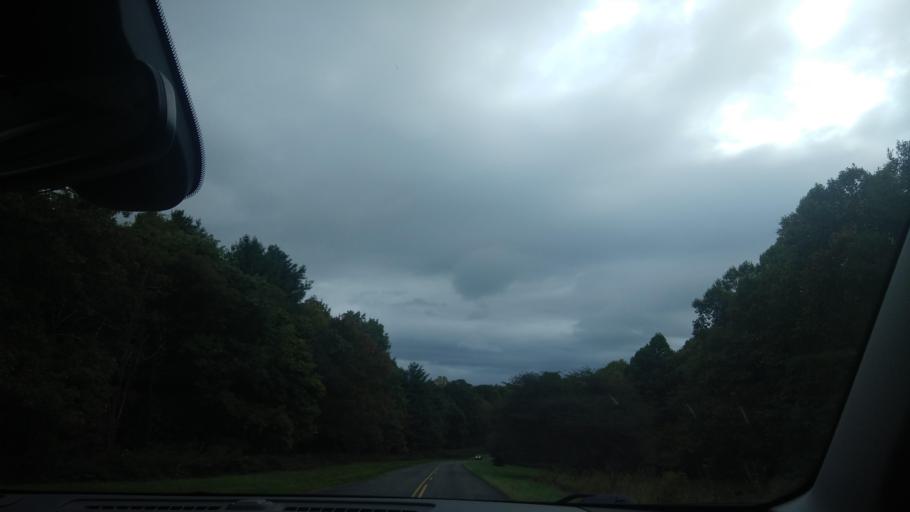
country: US
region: North Carolina
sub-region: Surry County
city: Flat Rock
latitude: 36.6429
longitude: -80.5468
